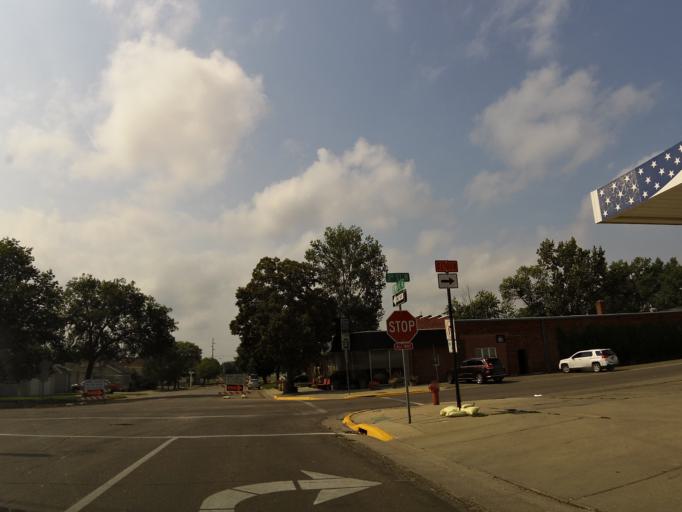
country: US
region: South Dakota
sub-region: Codington County
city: Watertown
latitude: 44.9014
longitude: -97.1192
